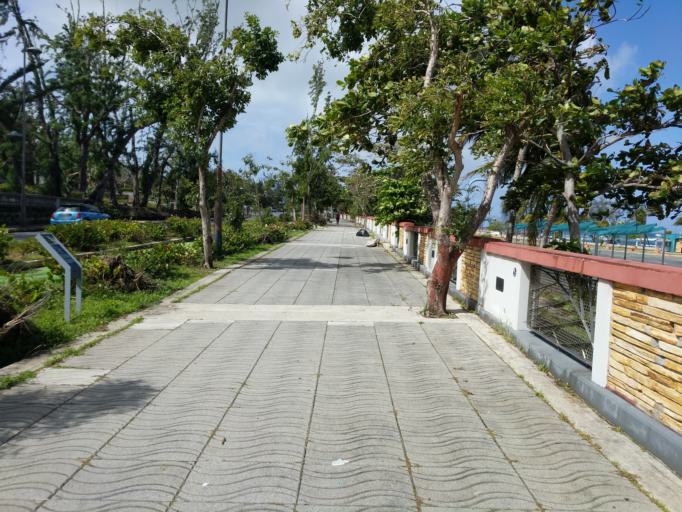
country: PR
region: San Juan
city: San Juan
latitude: 18.4655
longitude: -66.0912
